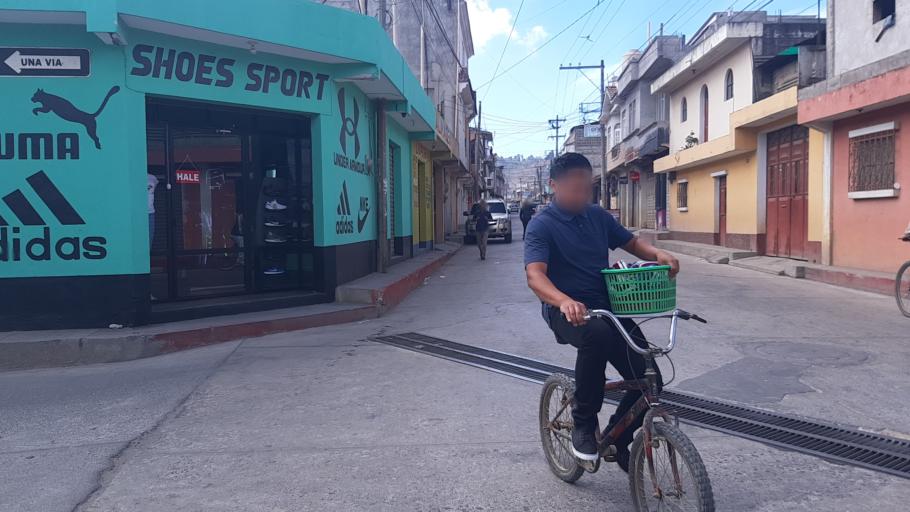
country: GT
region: Quetzaltenango
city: Ostuncalco
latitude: 14.8669
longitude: -91.6244
